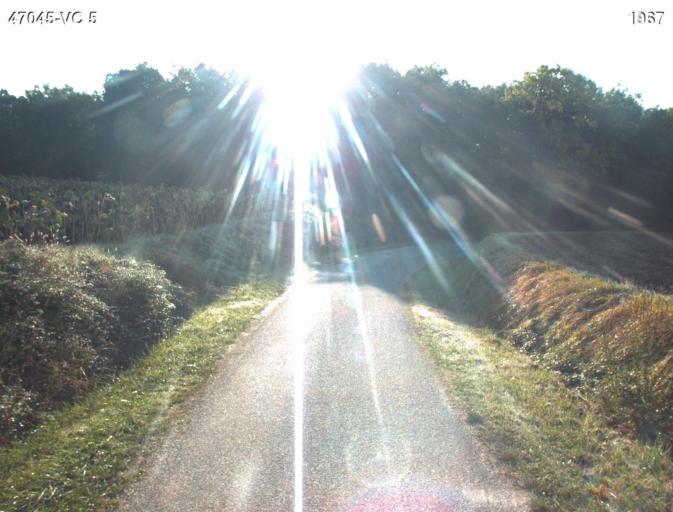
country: FR
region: Aquitaine
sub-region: Departement du Lot-et-Garonne
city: Nerac
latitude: 44.1461
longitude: 0.4054
